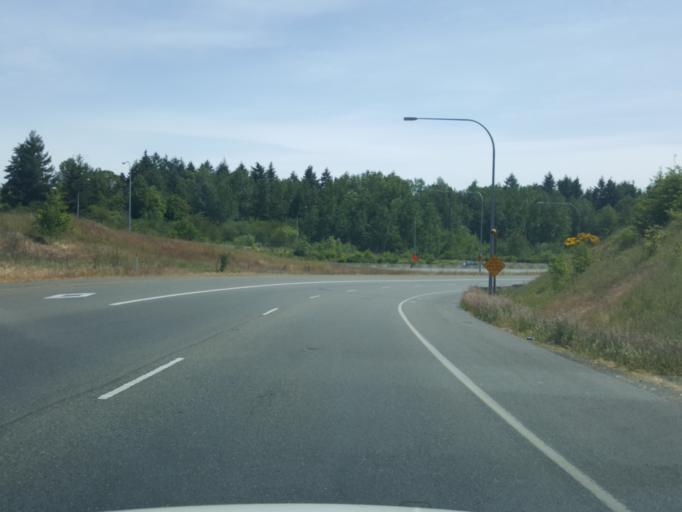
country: US
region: Washington
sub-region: Pierce County
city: Fircrest
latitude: 47.2405
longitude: -122.5042
